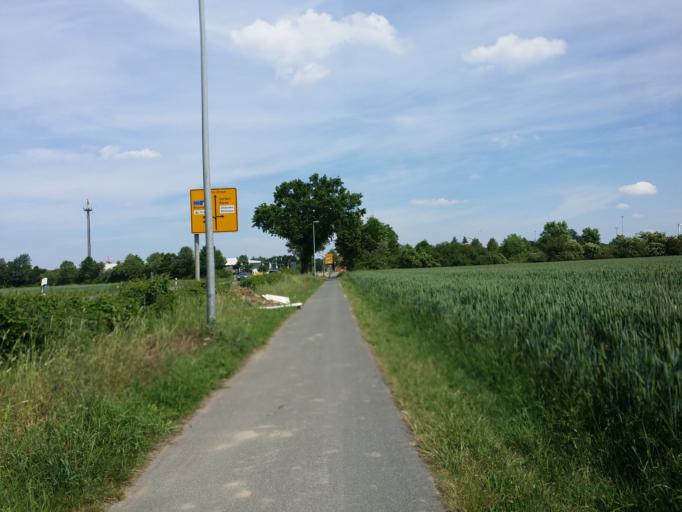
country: DE
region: Lower Saxony
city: Riede
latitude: 53.0080
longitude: 8.8763
